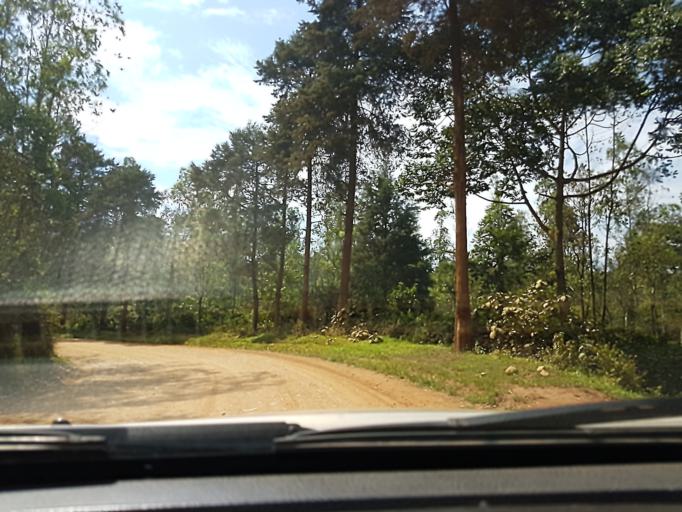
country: CD
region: South Kivu
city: Bukavu
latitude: -2.6431
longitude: 28.8758
